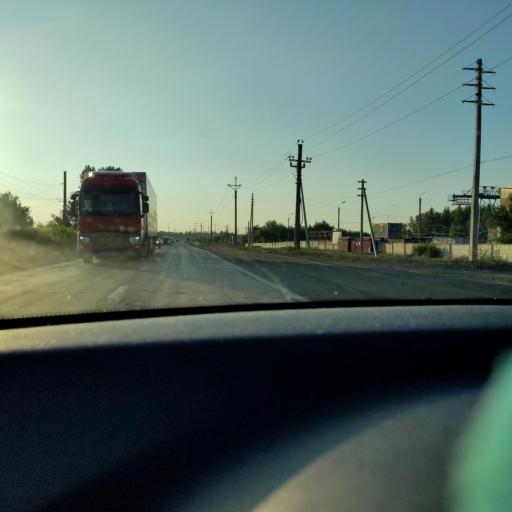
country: RU
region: Samara
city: Kinel'
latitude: 53.2338
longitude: 50.5854
